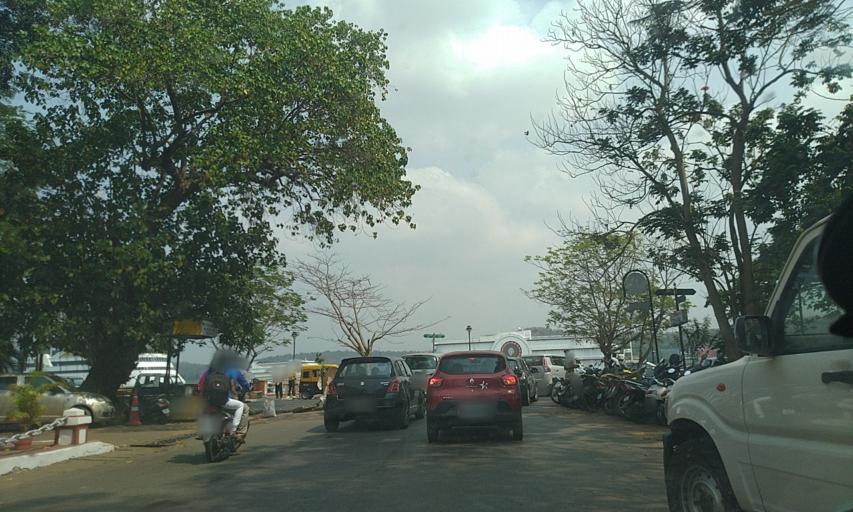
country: IN
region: Goa
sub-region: North Goa
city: Panaji
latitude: 15.5005
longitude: 73.8239
